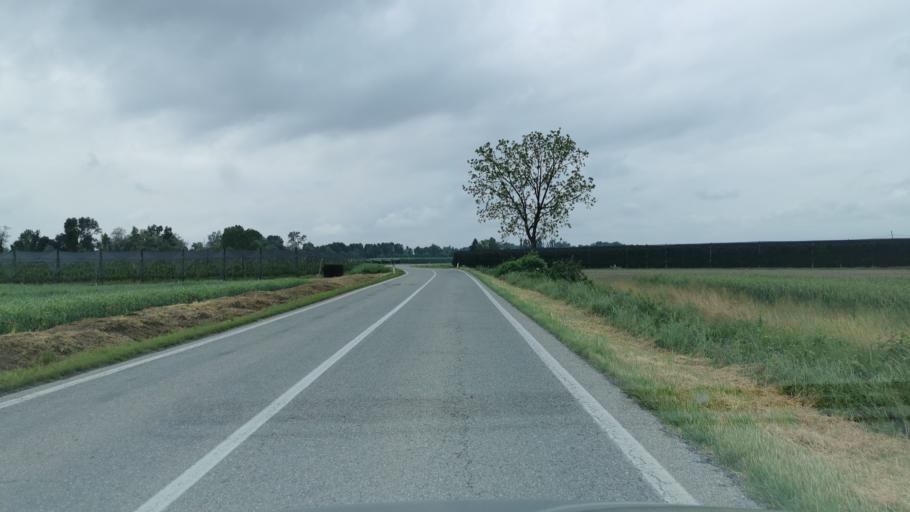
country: IT
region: Piedmont
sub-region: Provincia di Cuneo
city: Savigliano
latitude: 44.6187
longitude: 7.6300
